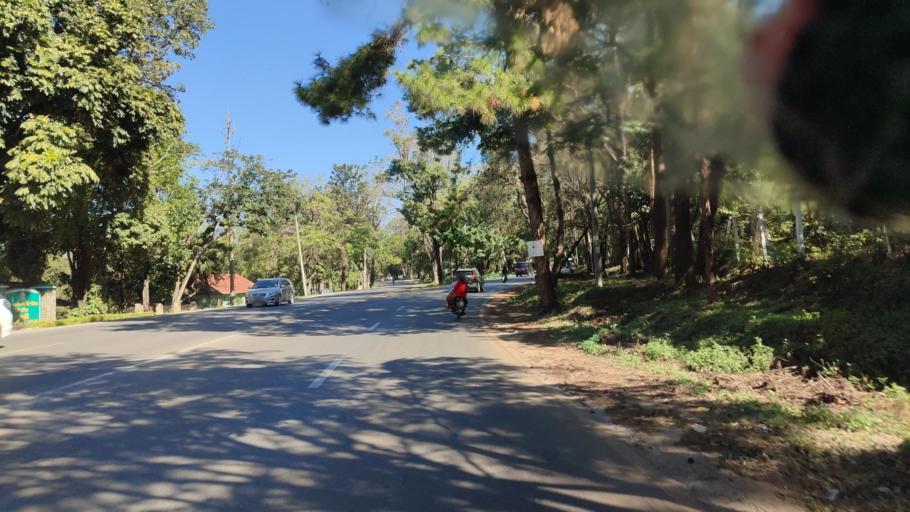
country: MM
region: Mandalay
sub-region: Pyin Oo Lwin District
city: Pyin Oo Lwin
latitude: 21.9903
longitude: 96.4208
